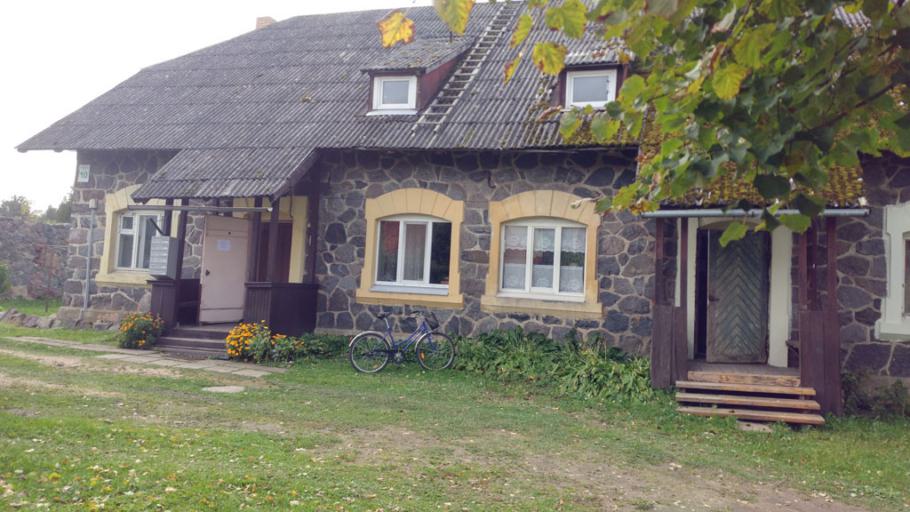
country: LV
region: Sigulda
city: Sigulda
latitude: 57.1665
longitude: 24.8280
